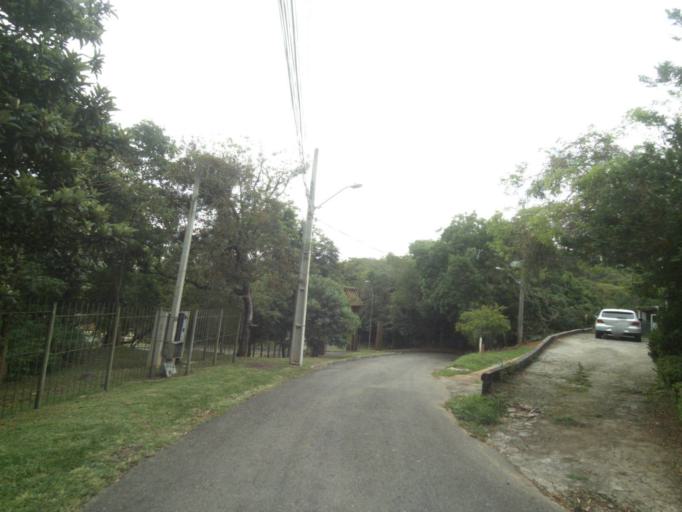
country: BR
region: Parana
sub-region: Curitiba
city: Curitiba
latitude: -25.4021
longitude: -49.2943
